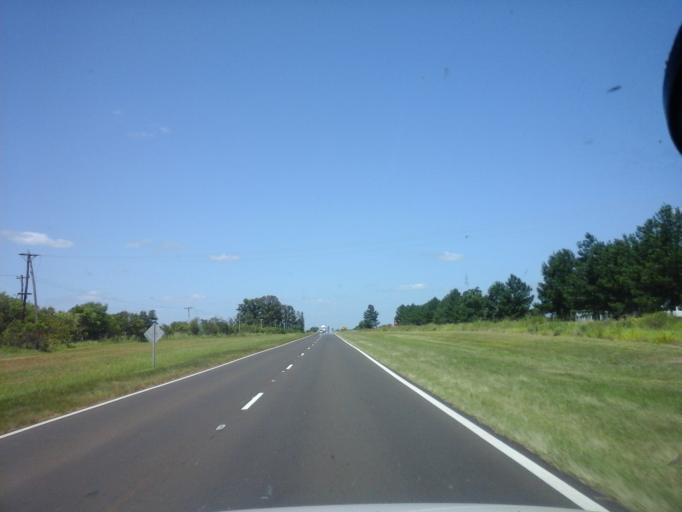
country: AR
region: Corrientes
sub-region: Departamento de Beron de Astrada
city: Beron de Astrada
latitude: -27.4665
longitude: -57.4713
